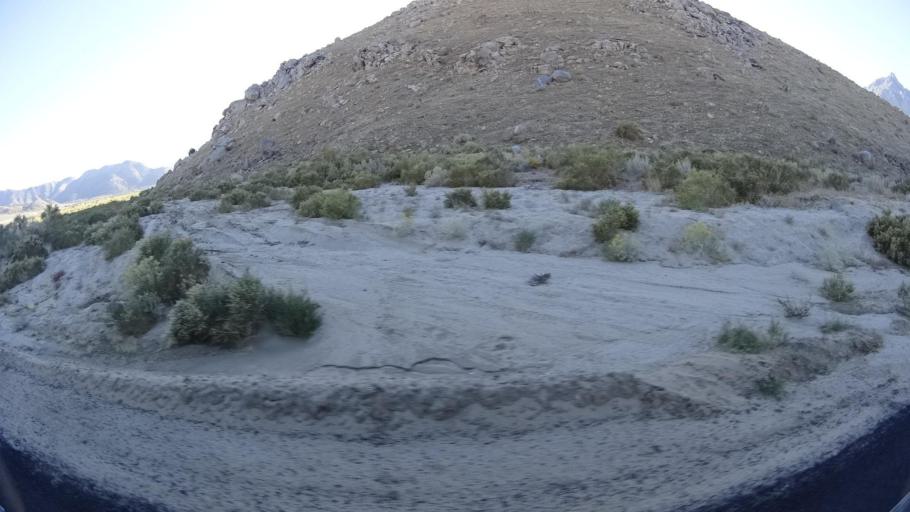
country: US
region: California
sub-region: Kern County
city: Weldon
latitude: 35.6147
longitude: -118.2488
